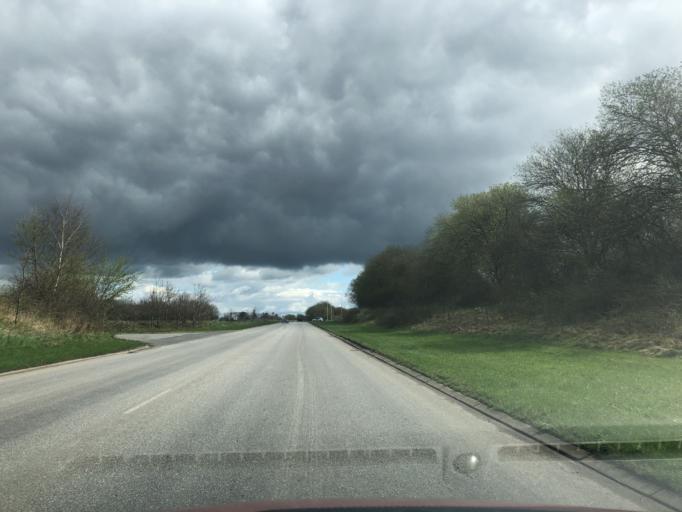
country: DK
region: South Denmark
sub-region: Kolding Kommune
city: Christiansfeld
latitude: 55.3638
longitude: 9.4924
